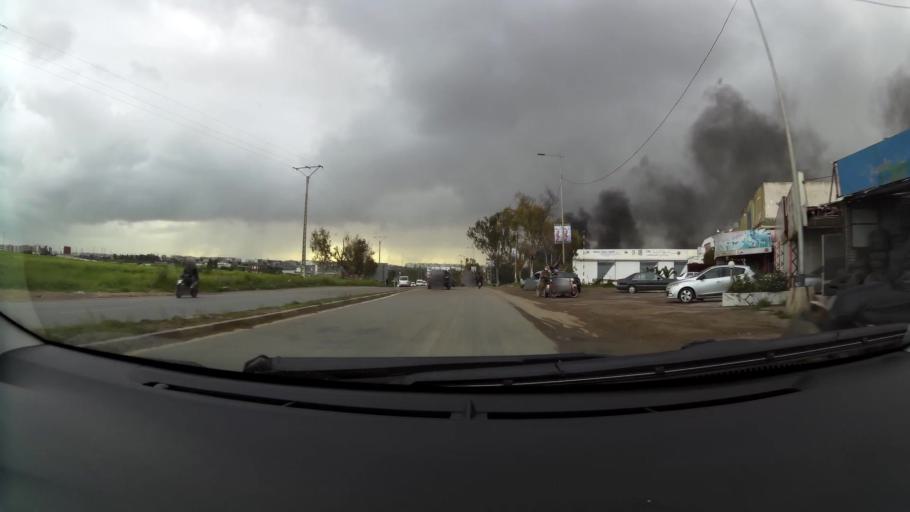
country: MA
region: Grand Casablanca
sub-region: Mediouna
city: Tit Mellil
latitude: 33.5654
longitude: -7.5005
